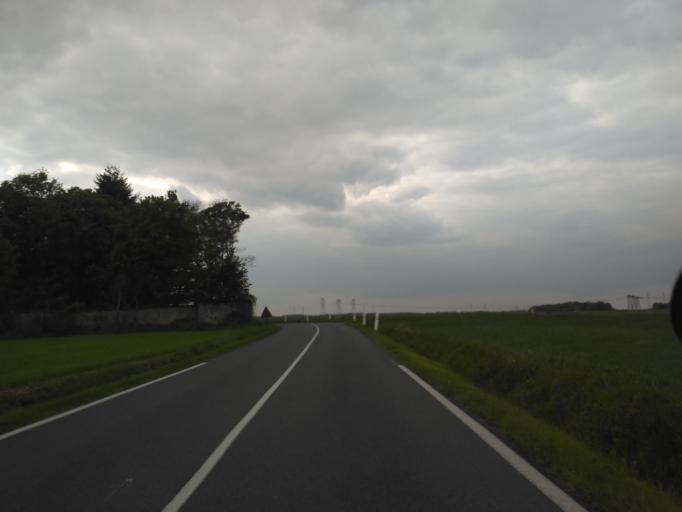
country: FR
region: Ile-de-France
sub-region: Departement de Seine-et-Marne
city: Rubelles
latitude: 48.5658
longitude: 2.6894
